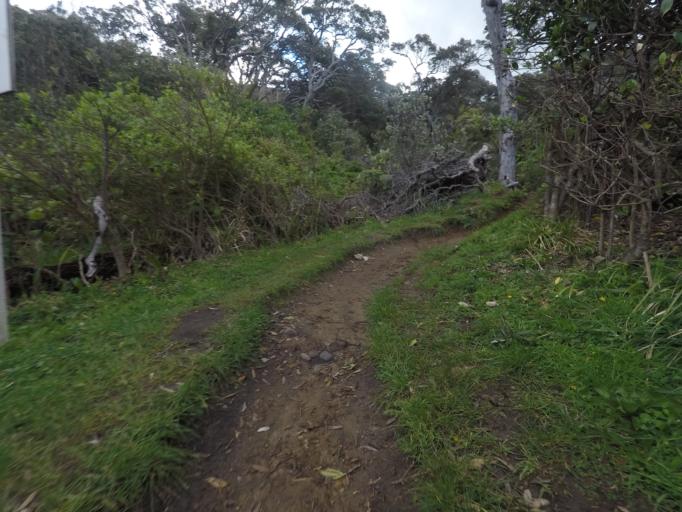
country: NZ
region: Bay of Plenty
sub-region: Western Bay of Plenty District
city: Waihi Beach
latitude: -37.3863
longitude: 175.9392
